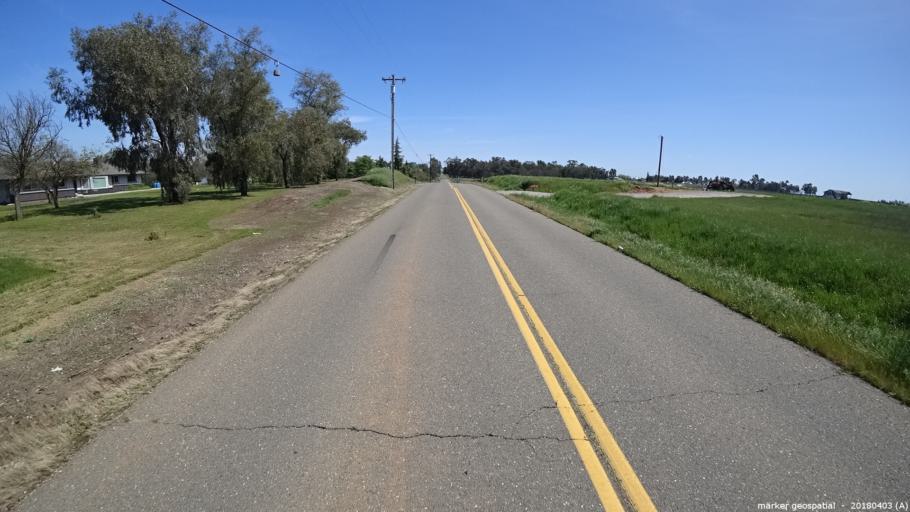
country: US
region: California
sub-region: Sacramento County
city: Wilton
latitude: 38.3796
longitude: -121.2300
